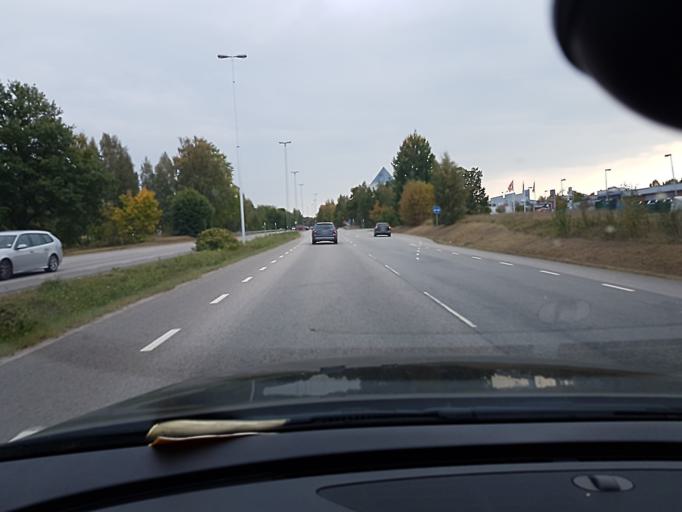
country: SE
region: Kronoberg
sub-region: Vaxjo Kommun
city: Vaexjoe
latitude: 56.8560
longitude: 14.8217
